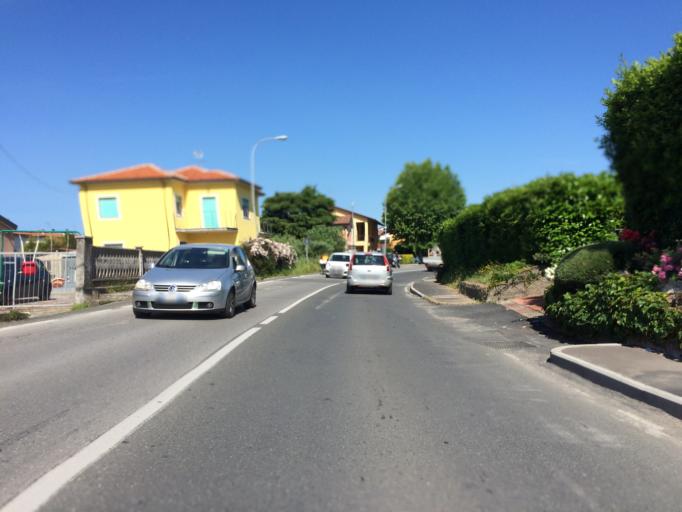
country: IT
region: Tuscany
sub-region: Provincia di Massa-Carrara
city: Borghetto-Melara
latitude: 44.0916
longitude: 9.9948
